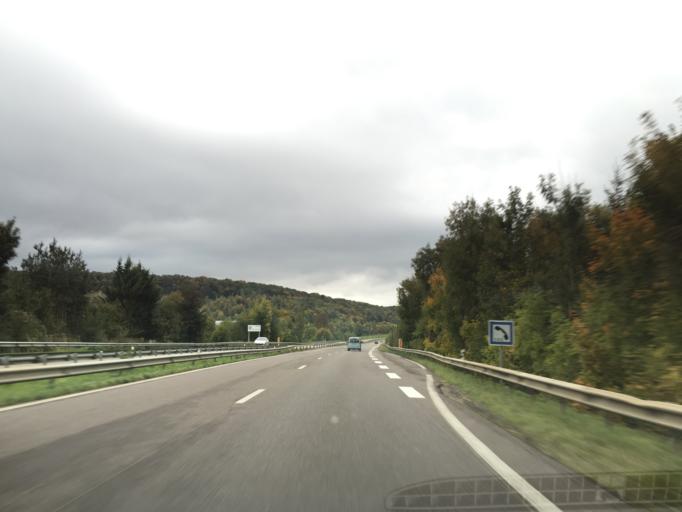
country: FR
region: Lorraine
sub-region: Departement de la Meuse
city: Vacon
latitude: 48.6873
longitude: 5.6625
